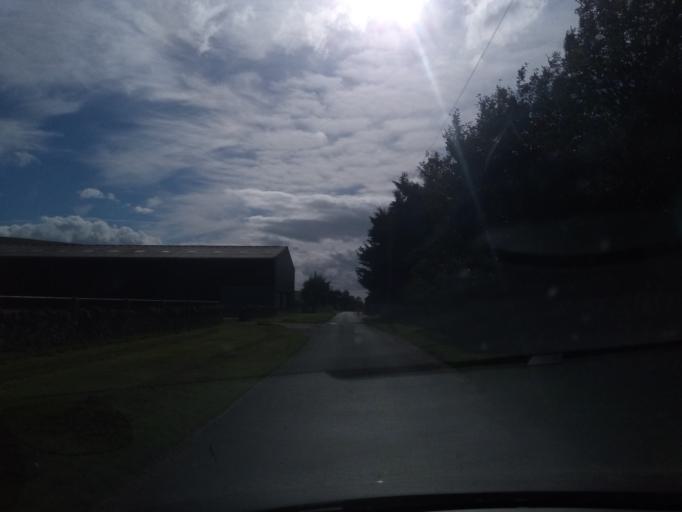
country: GB
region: Scotland
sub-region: The Scottish Borders
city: Coldstream
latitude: 55.6170
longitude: -2.1950
